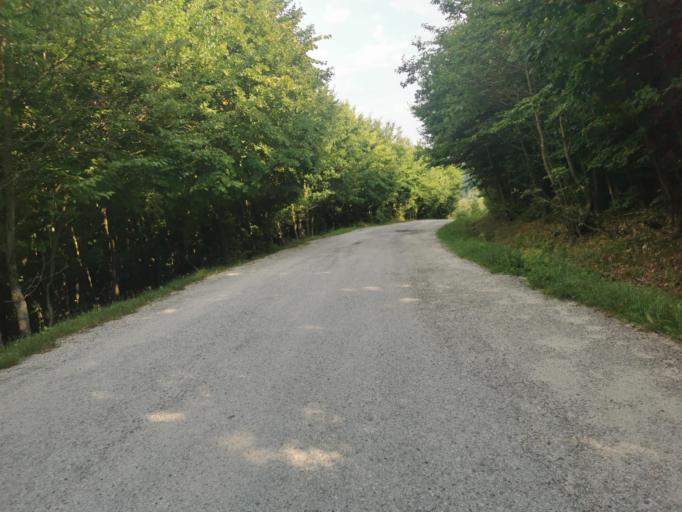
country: SK
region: Nitriansky
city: Stara Tura
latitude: 48.8119
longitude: 17.6327
